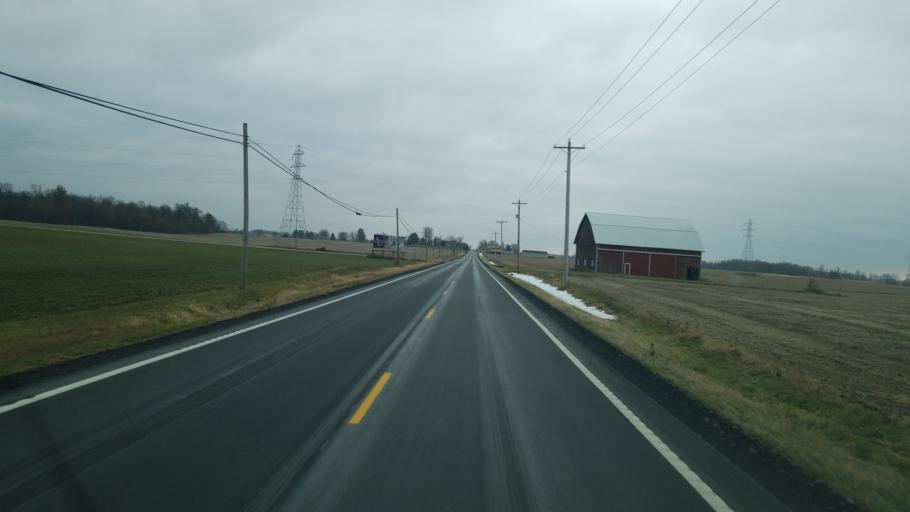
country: US
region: Ohio
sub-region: Crawford County
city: Bucyrus
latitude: 40.8501
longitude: -82.9676
